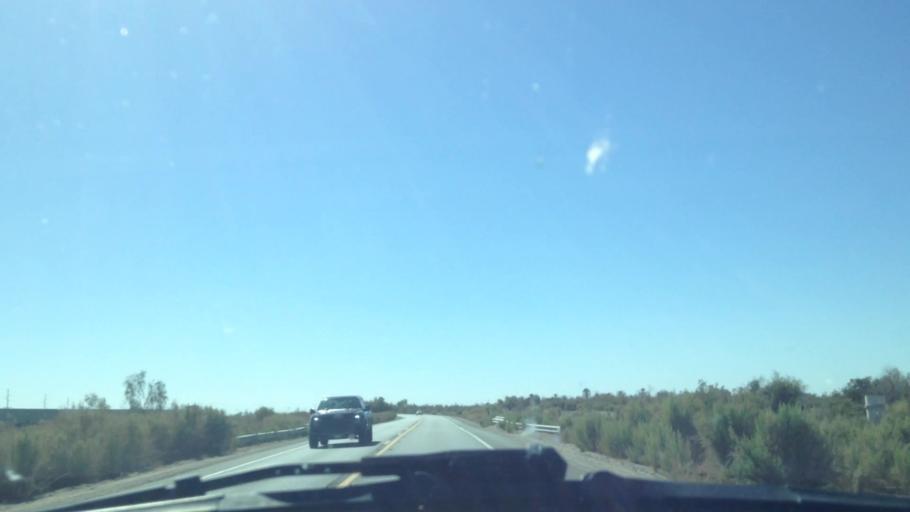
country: US
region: California
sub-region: Riverside County
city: Mecca
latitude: 33.5608
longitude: -116.0706
